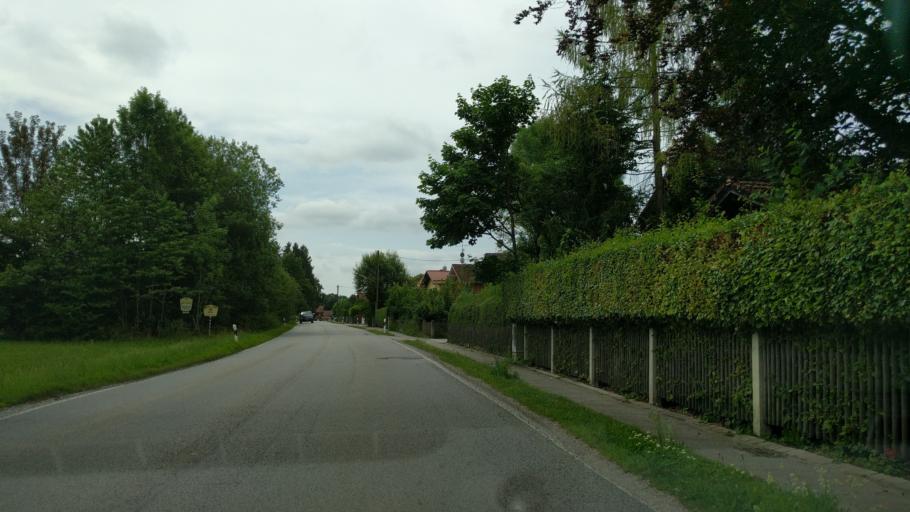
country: DE
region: Bavaria
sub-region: Upper Bavaria
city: Strasslach-Dingharting
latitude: 48.0084
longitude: 11.5144
